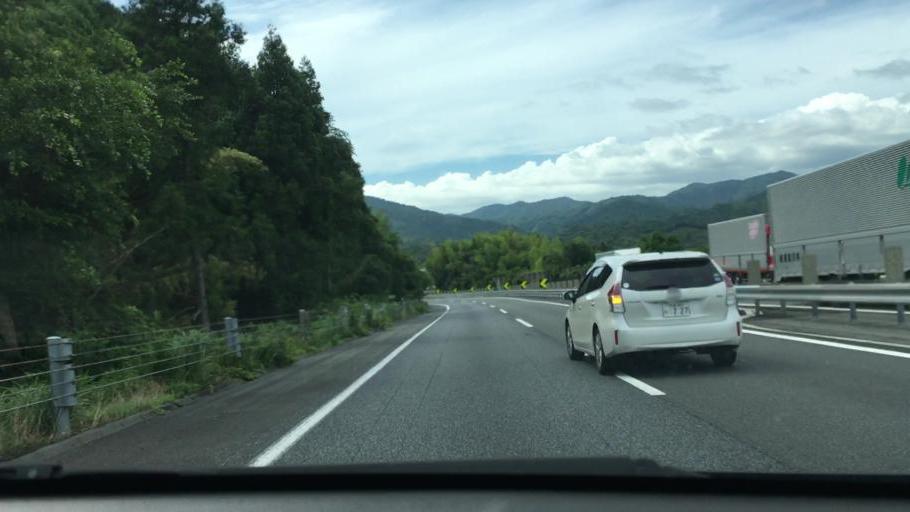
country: JP
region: Yamaguchi
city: Ogori-shimogo
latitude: 34.1309
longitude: 131.4339
